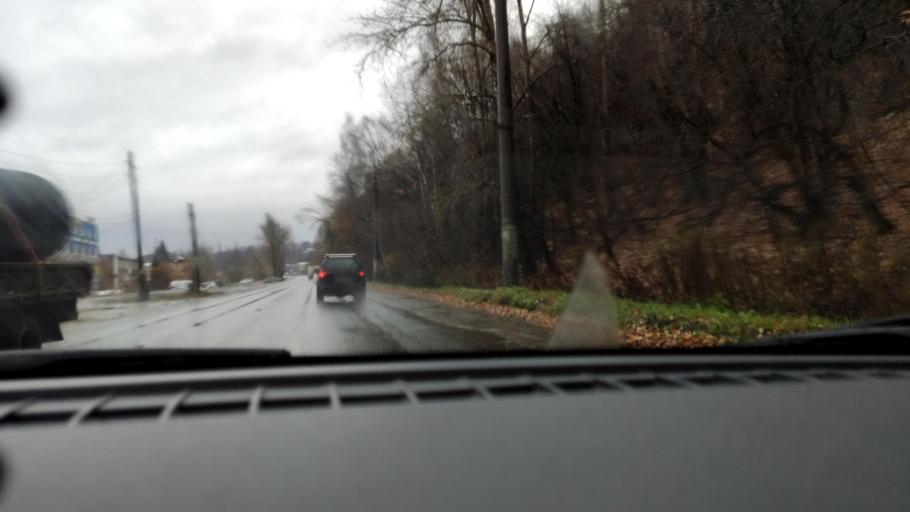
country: RU
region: Perm
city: Perm
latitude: 58.0670
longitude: 56.3443
